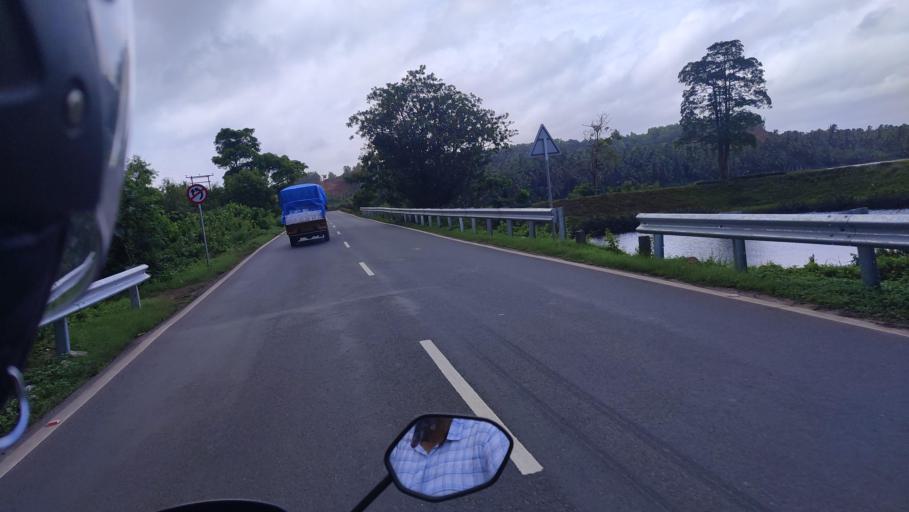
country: IN
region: Kerala
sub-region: Kasaragod District
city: Nileshwar
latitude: 12.2360
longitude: 75.1508
